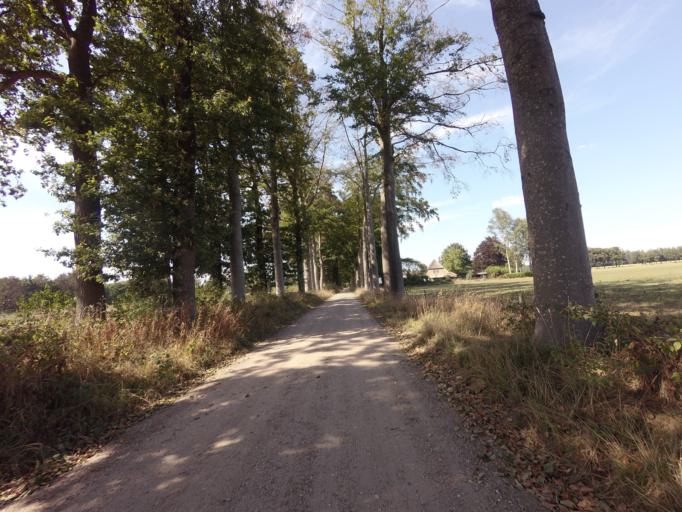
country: NL
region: Gelderland
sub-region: Gemeente Apeldoorn
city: Loenen
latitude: 52.1348
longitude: 6.0327
